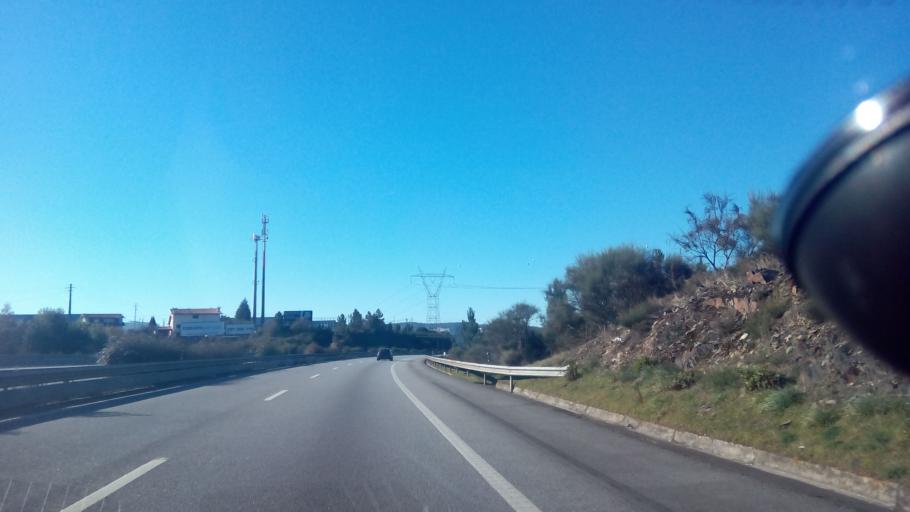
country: PT
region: Porto
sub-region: Paredes
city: Recarei
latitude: 41.1735
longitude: -8.4261
